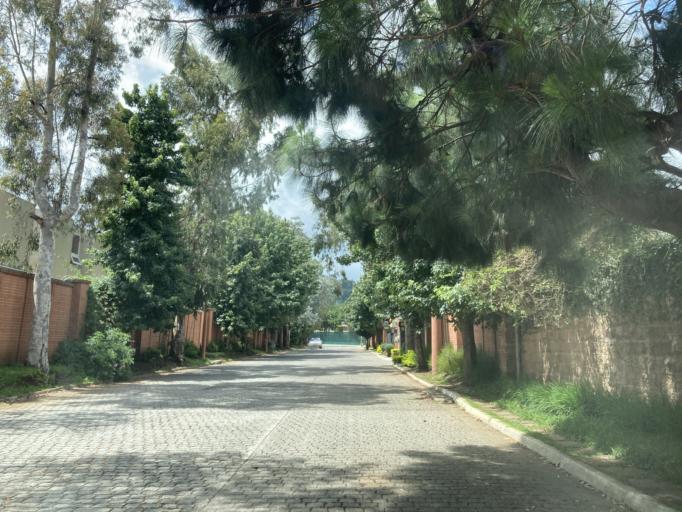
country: GT
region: Guatemala
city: San Jose Pinula
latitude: 14.5409
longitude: -90.4353
